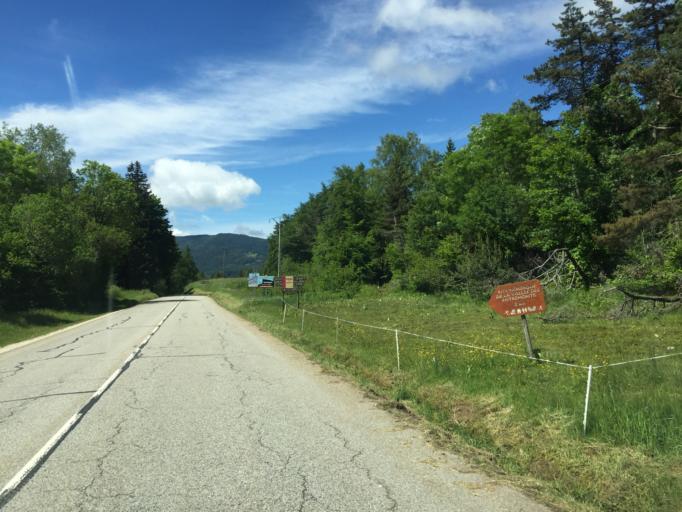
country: FR
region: Rhone-Alpes
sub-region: Departement de la Savoie
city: Saint-Baldoph
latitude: 45.4800
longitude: 5.9143
